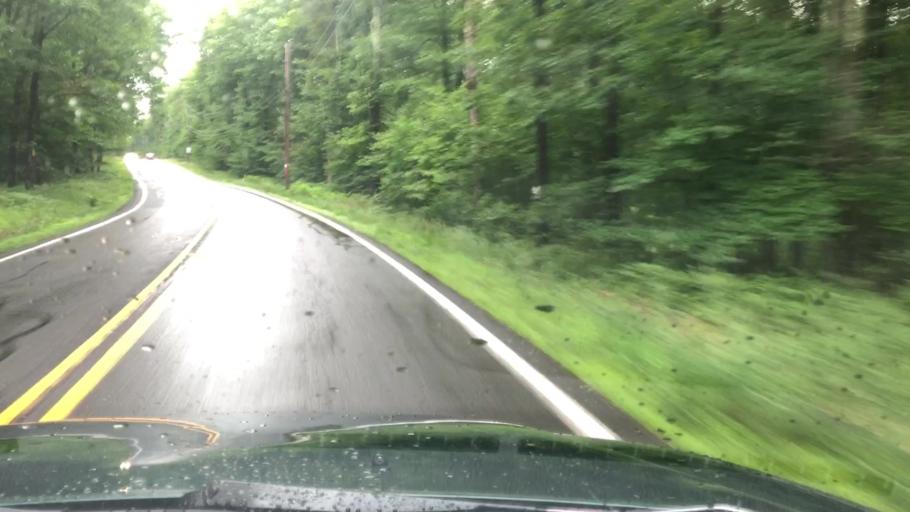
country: US
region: Pennsylvania
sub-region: Monroe County
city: Mountainhome
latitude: 41.2595
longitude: -75.2324
